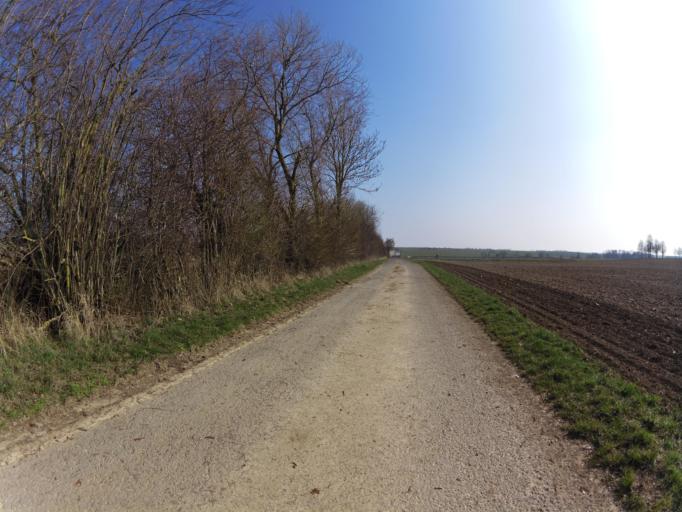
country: DE
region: Bavaria
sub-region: Regierungsbezirk Unterfranken
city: Sulzdorf
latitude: 49.6571
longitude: 9.9147
